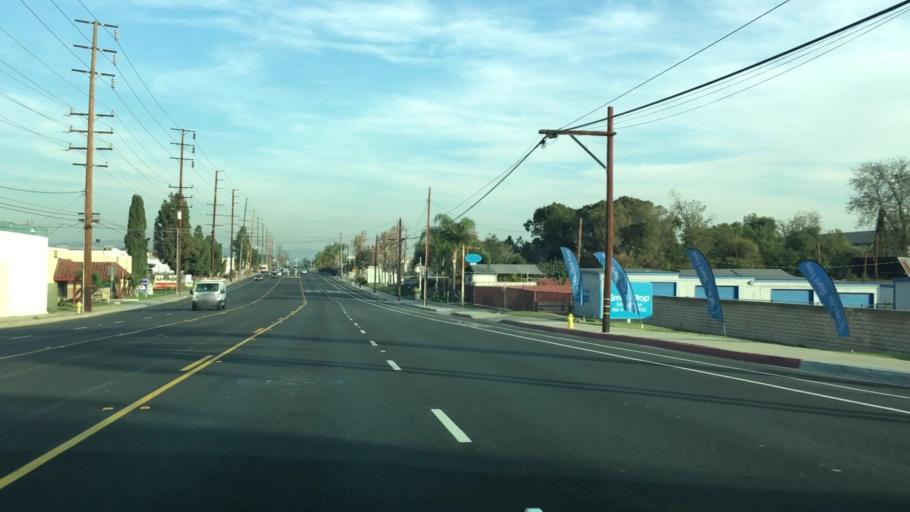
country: US
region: California
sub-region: Orange County
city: La Habra
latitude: 33.9246
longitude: -117.9403
